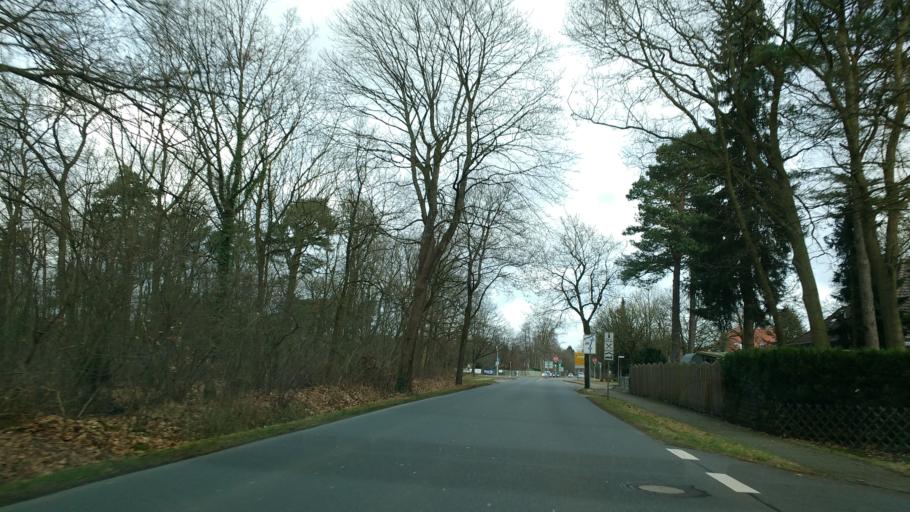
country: DE
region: Lower Saxony
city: Hambuhren
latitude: 52.6321
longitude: 9.9300
